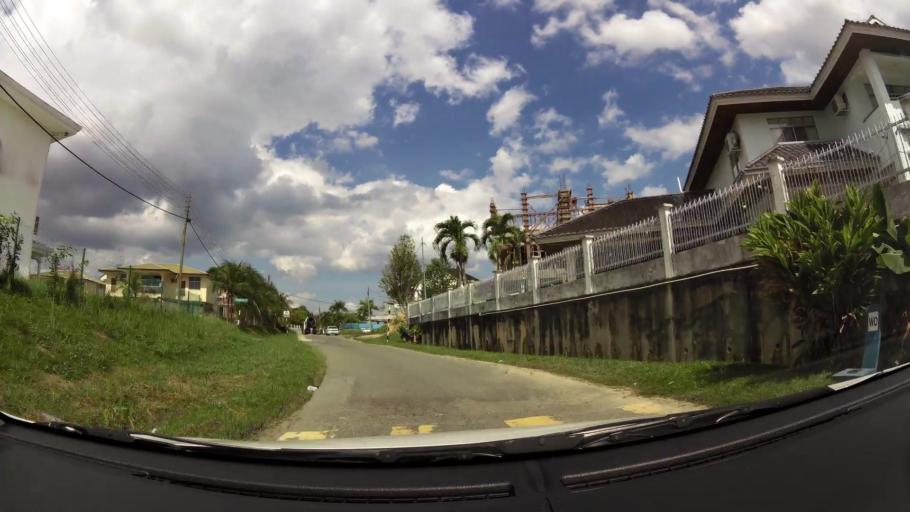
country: BN
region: Brunei and Muara
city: Bandar Seri Begawan
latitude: 4.9556
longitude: 114.9613
